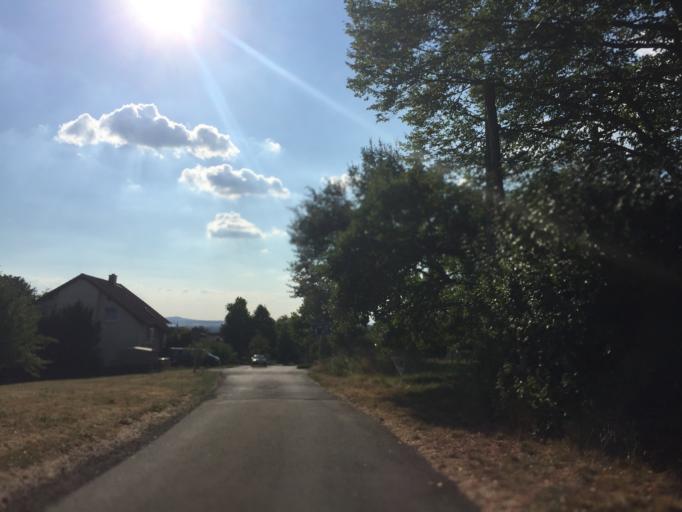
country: DE
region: Hesse
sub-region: Regierungsbezirk Giessen
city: Langgons
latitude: 50.5330
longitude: 8.7213
